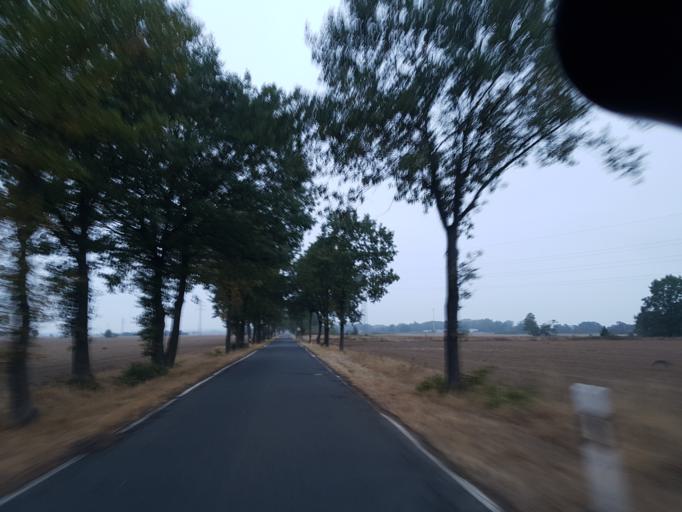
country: DE
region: Saxony-Anhalt
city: Annaburg
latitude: 51.7713
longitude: 13.0665
